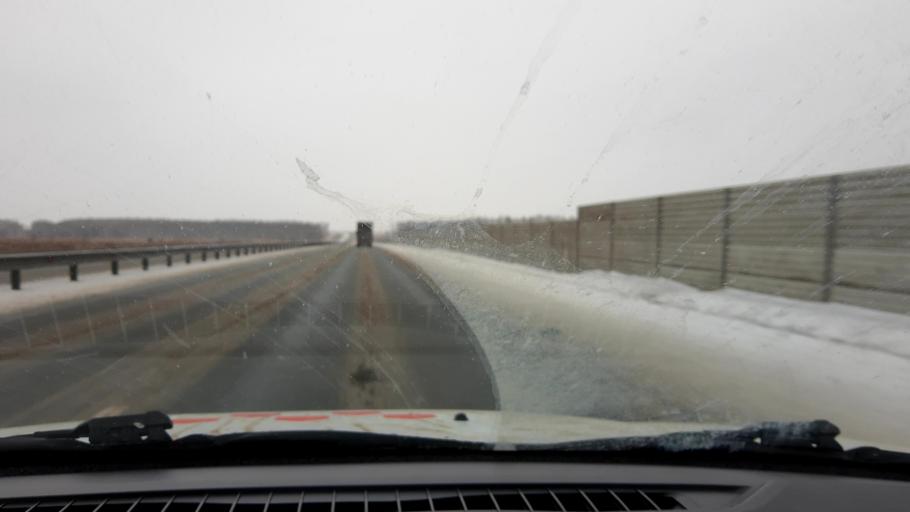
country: RU
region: Nizjnij Novgorod
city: Burevestnik
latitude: 56.1116
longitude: 43.9712
